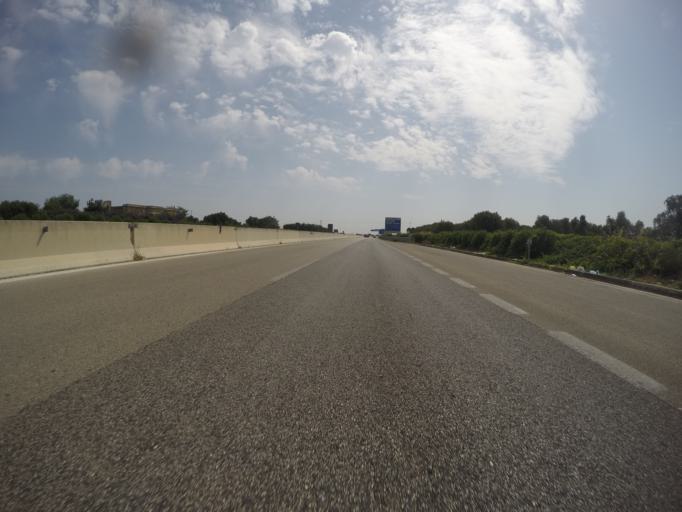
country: IT
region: Apulia
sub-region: Provincia di Brindisi
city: Latiano
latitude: 40.5466
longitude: 17.6957
